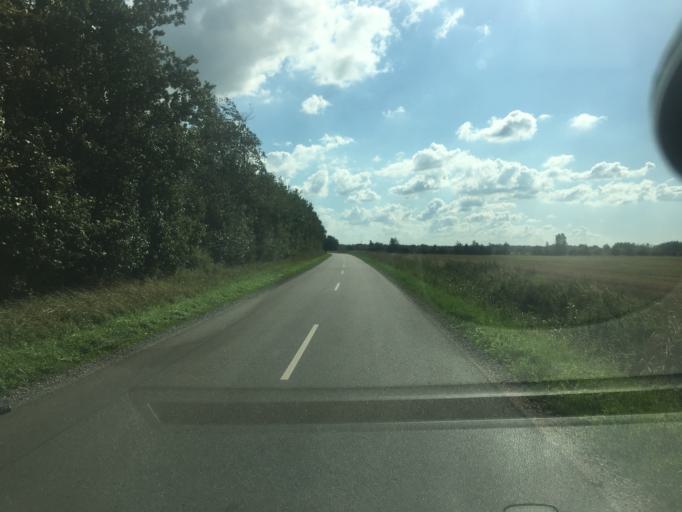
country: DE
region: Schleswig-Holstein
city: Ellhoft
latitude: 54.9666
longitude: 8.9640
